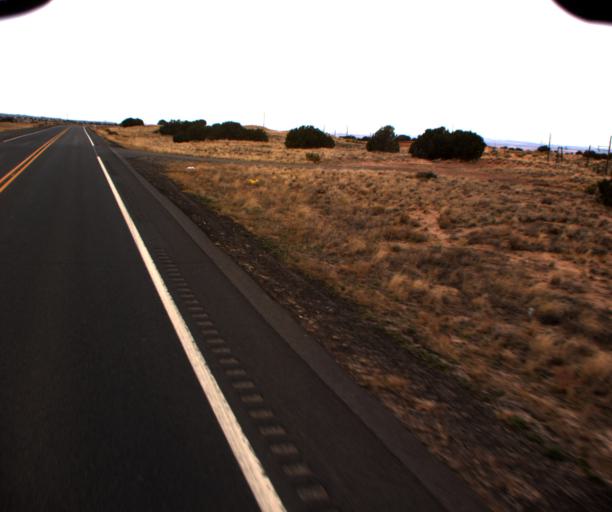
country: US
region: Arizona
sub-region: Coconino County
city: Kaibito
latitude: 36.4427
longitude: -110.7360
